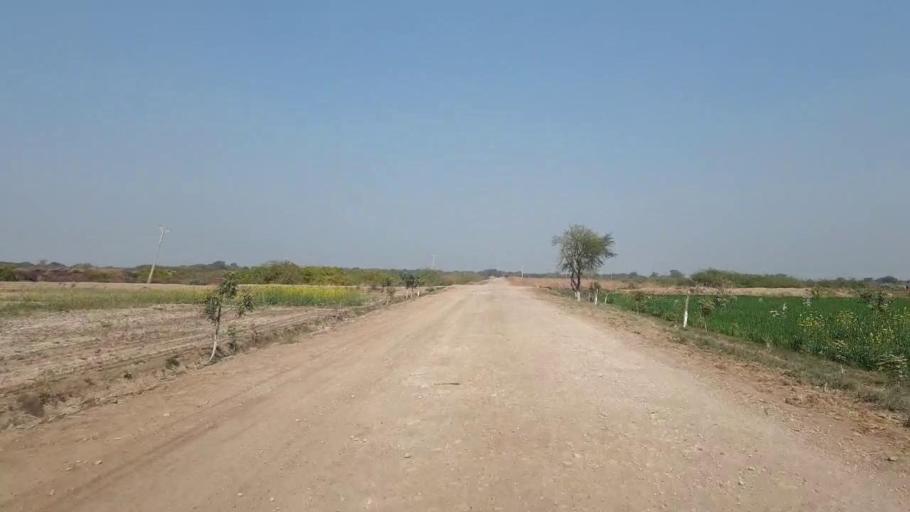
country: PK
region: Sindh
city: Mirwah Gorchani
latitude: 25.3772
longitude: 68.9317
